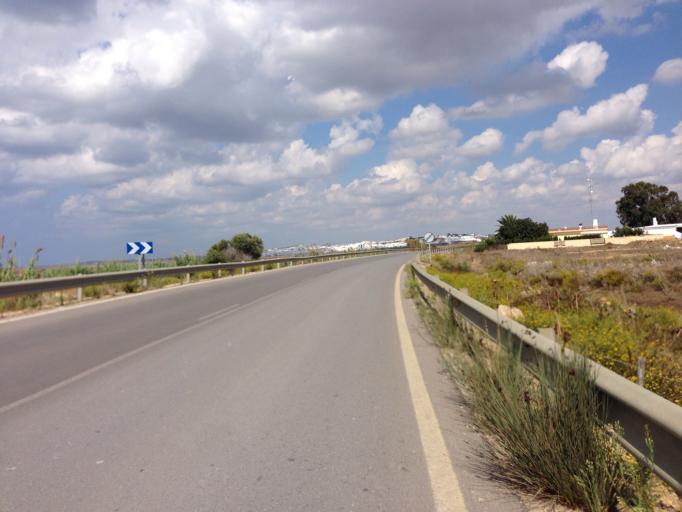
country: ES
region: Andalusia
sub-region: Provincia de Cadiz
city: Conil de la Frontera
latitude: 36.2512
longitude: -6.0685
